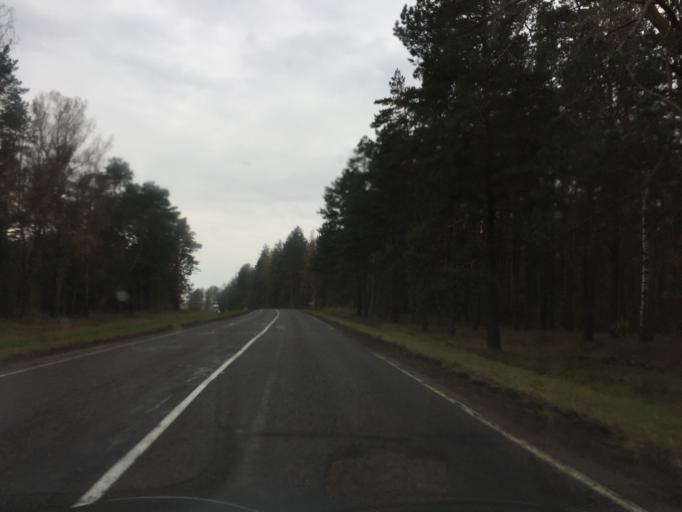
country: BY
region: Gomel
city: Dowsk
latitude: 53.1944
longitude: 30.5123
